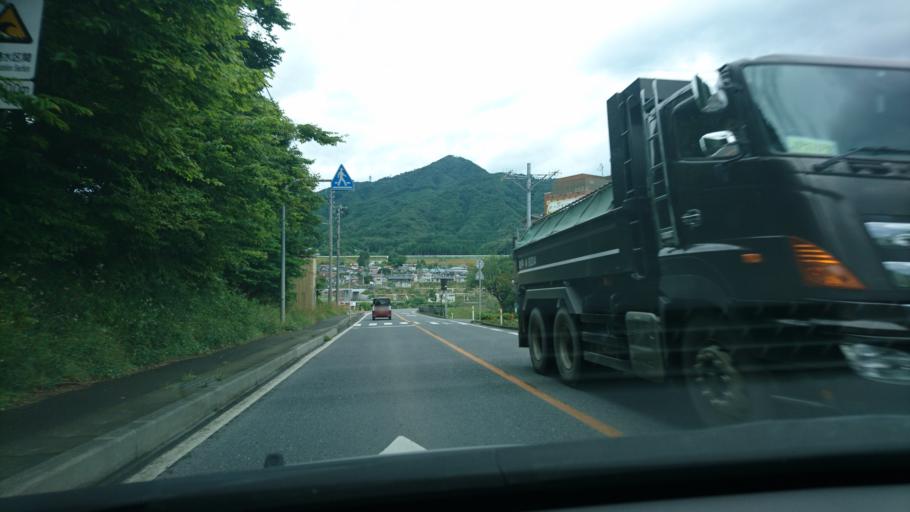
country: JP
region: Iwate
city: Otsuchi
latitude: 39.3802
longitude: 141.9389
